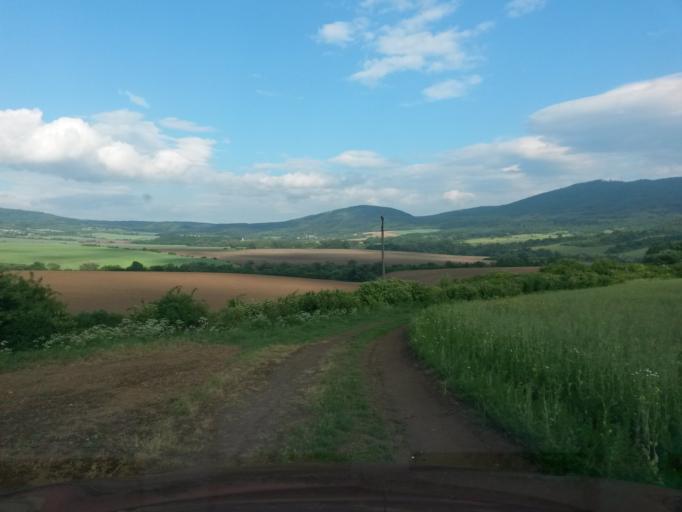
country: SK
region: Kosicky
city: Secovce
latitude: 48.7463
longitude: 21.4627
